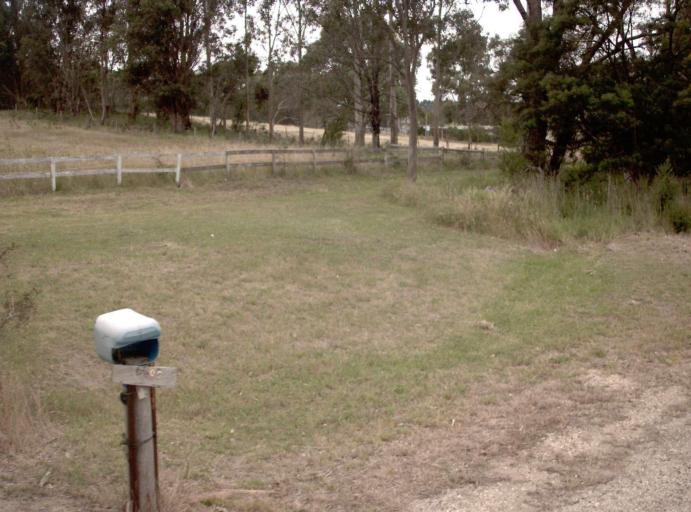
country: AU
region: Victoria
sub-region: Wellington
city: Sale
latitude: -38.1798
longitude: 147.1318
